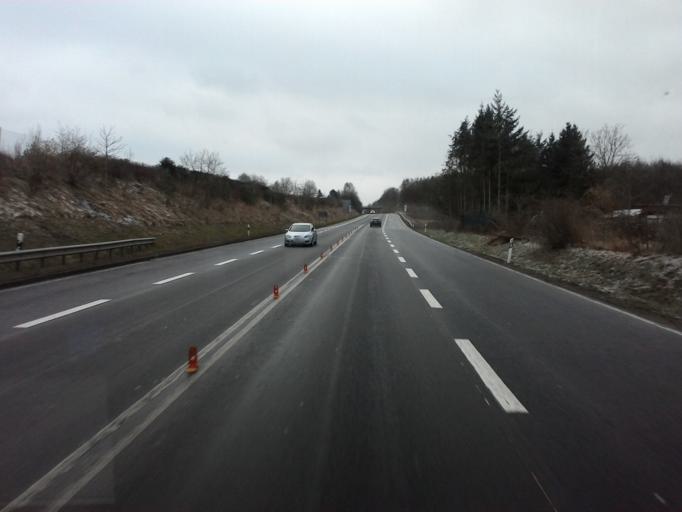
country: DE
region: Rheinland-Pfalz
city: Bitburg
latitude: 49.9682
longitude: 6.5139
